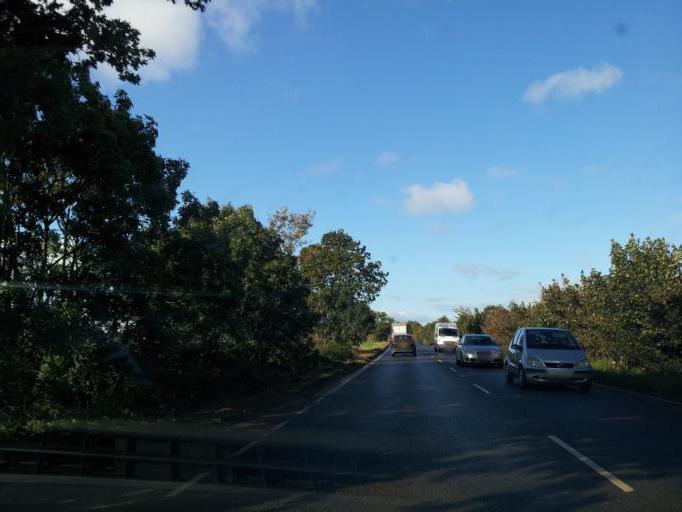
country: GB
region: England
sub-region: Norfolk
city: King's Lynn
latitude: 52.7159
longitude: 0.4854
